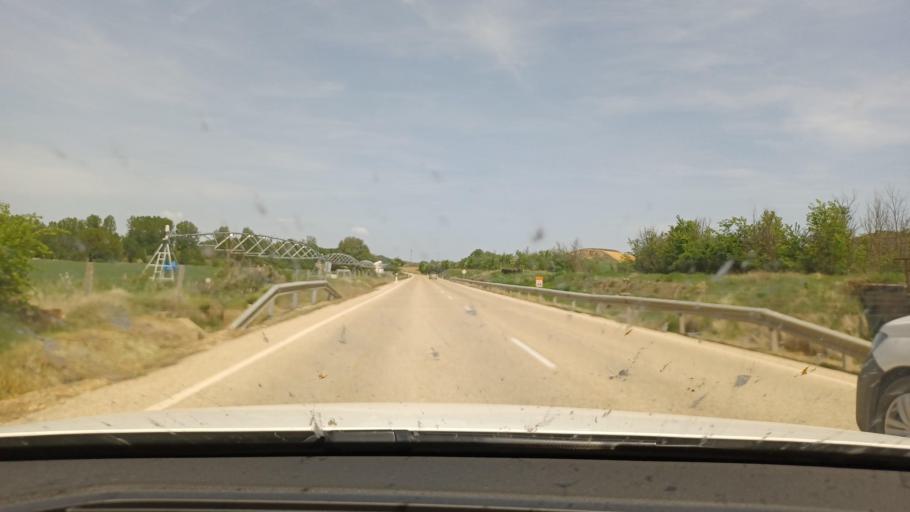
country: ES
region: Castille and Leon
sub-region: Provincia de Soria
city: Almazan
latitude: 41.4729
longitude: -2.5661
